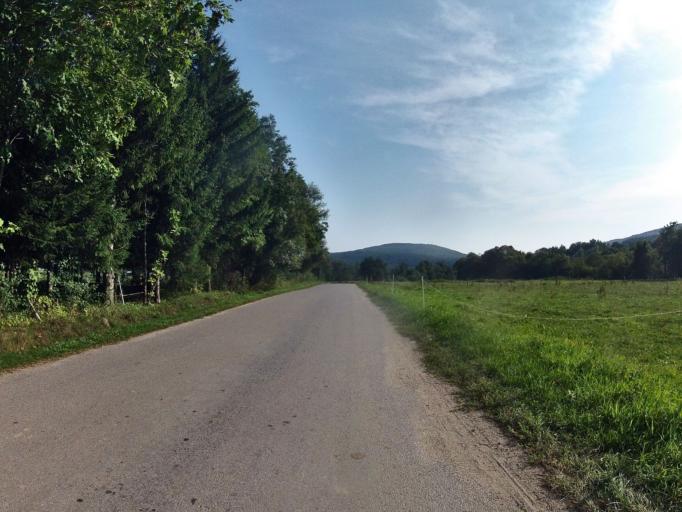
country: PL
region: Subcarpathian Voivodeship
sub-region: Powiat jasielski
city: Krempna
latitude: 49.5375
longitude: 21.5489
